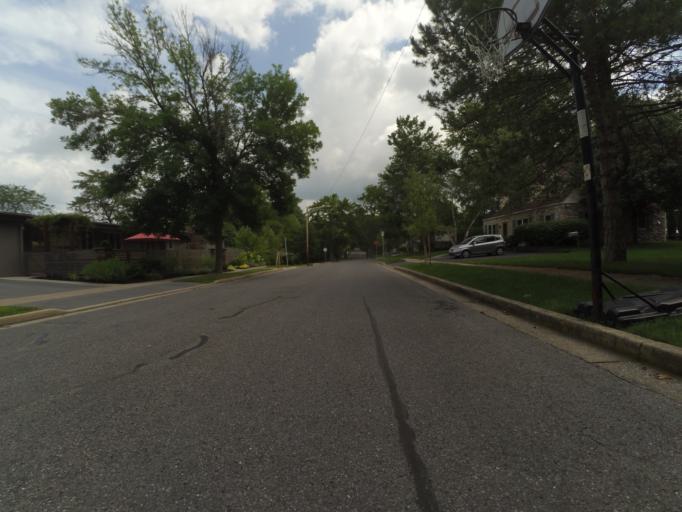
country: US
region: Pennsylvania
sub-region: Centre County
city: State College
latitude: 40.7870
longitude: -77.8482
